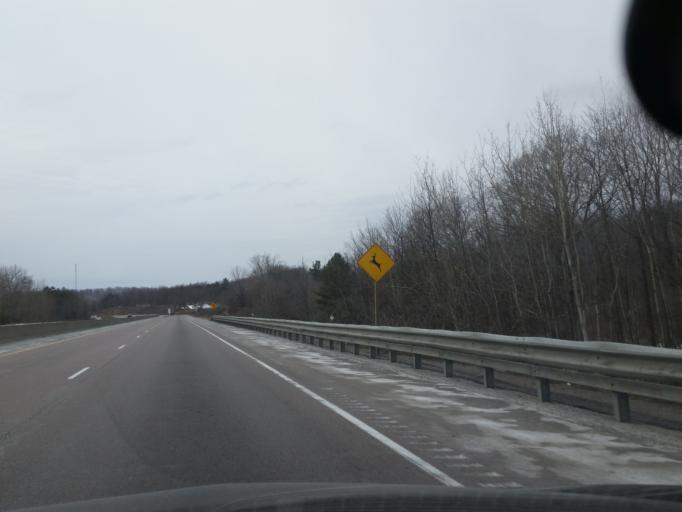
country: CA
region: Ontario
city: Quinte West
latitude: 44.1181
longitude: -77.6343
